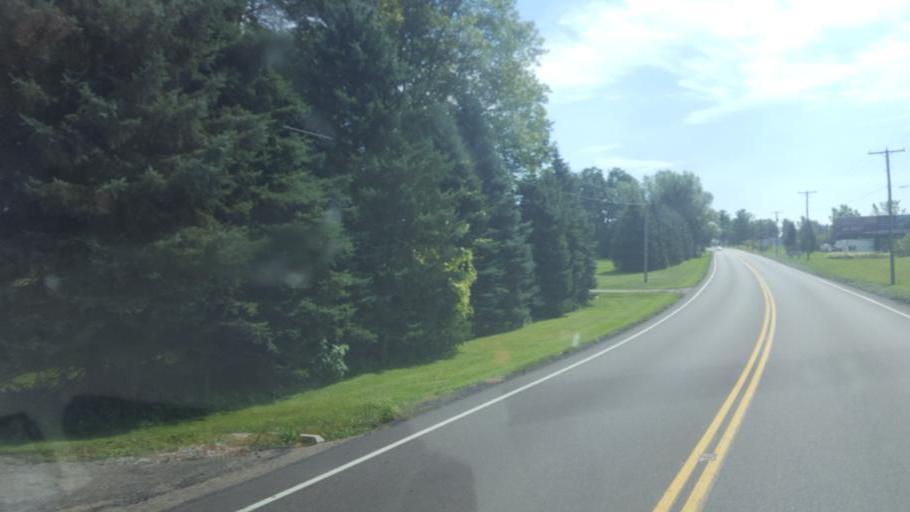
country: US
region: Ohio
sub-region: Knox County
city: Mount Vernon
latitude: 40.4135
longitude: -82.4996
